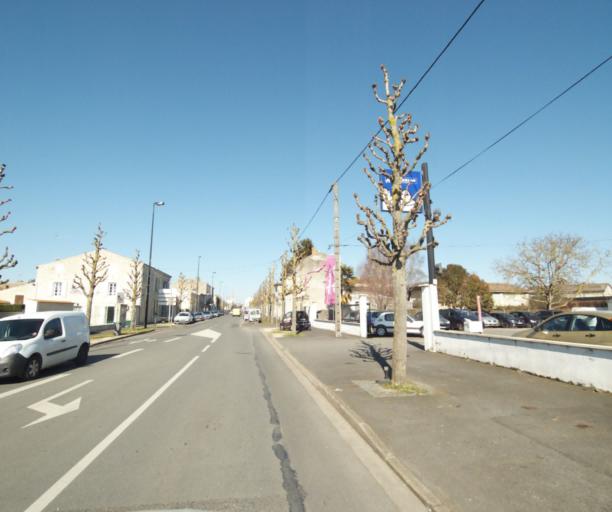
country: FR
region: Poitou-Charentes
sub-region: Departement des Deux-Sevres
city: Niort
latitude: 46.3107
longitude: -0.4656
